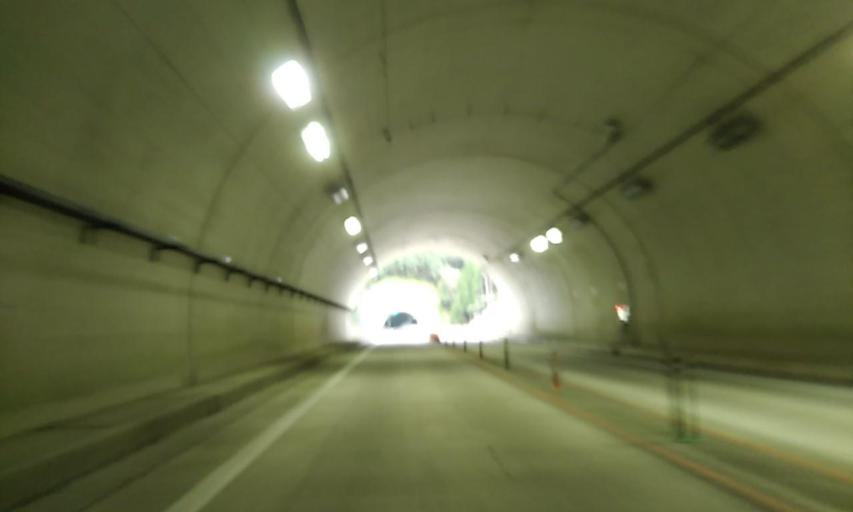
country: JP
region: Wakayama
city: Shingu
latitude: 33.6338
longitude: 135.9245
